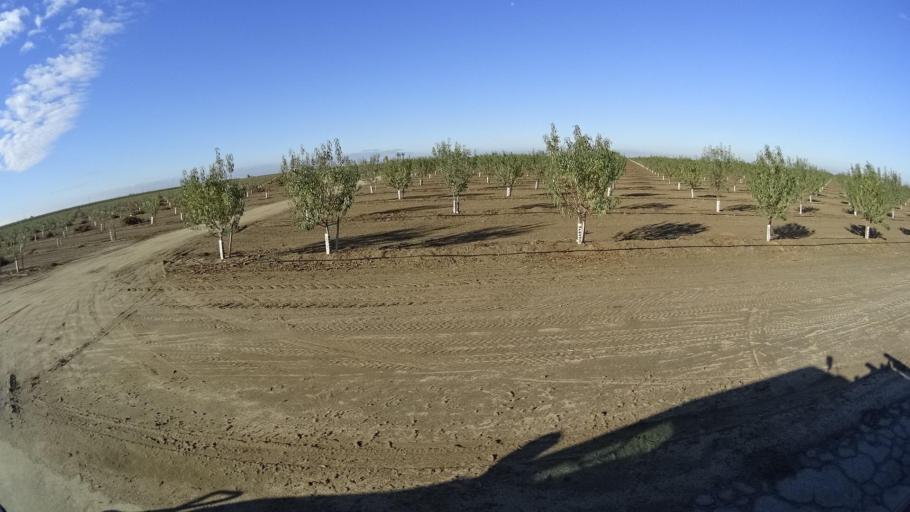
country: US
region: California
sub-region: Kern County
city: Delano
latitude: 35.7143
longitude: -119.2941
